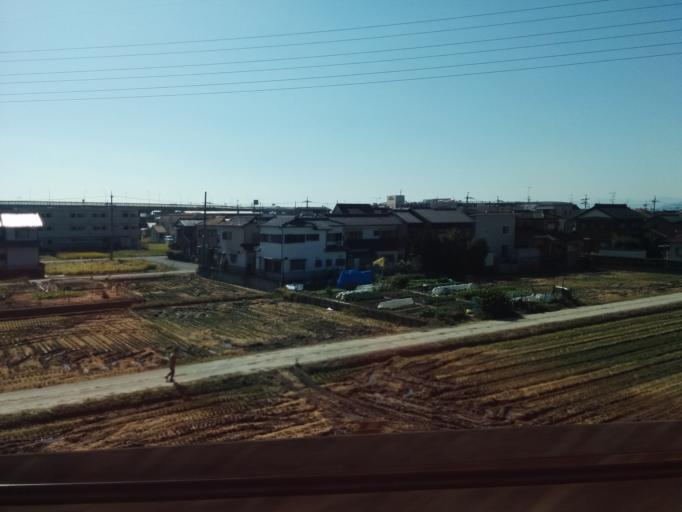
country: JP
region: Aichi
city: Inazawa
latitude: 35.2222
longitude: 136.8340
